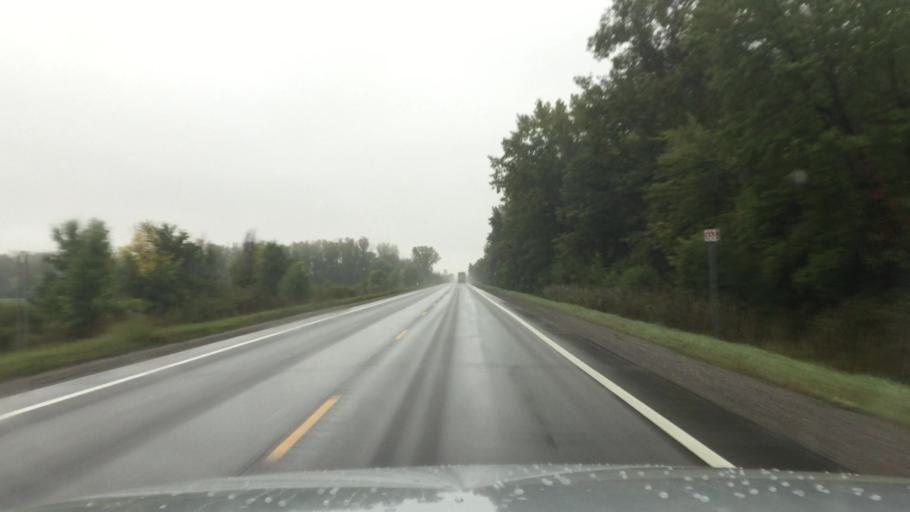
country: US
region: Michigan
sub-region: Saginaw County
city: Saginaw
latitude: 43.3718
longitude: -83.9551
